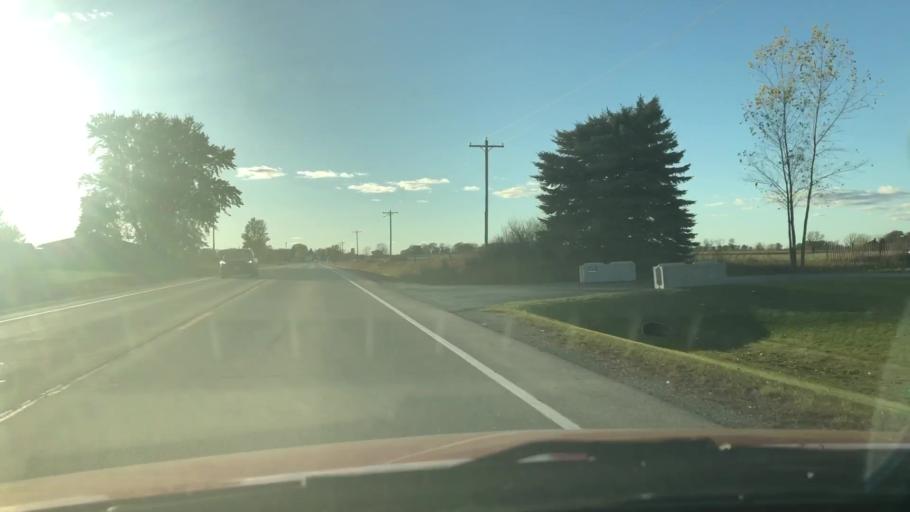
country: US
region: Wisconsin
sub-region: Brown County
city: Oneida
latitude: 44.4447
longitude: -88.1447
